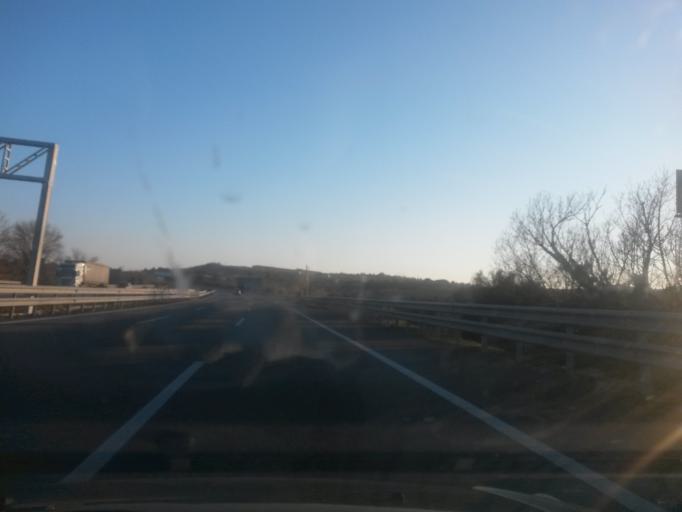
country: ES
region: Catalonia
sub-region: Provincia de Girona
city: Pont de Molins
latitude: 42.2943
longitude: 2.9405
